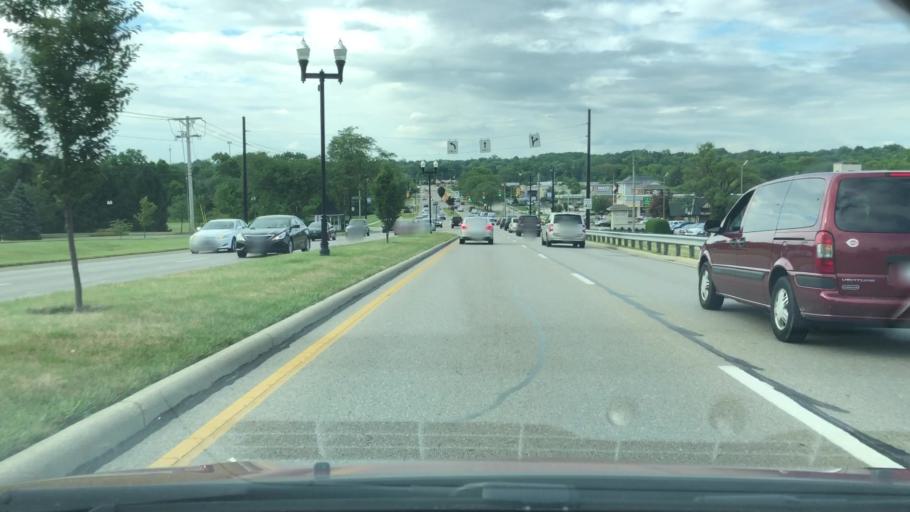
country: US
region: Ohio
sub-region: Montgomery County
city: Centerville
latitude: 39.6517
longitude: -84.1570
